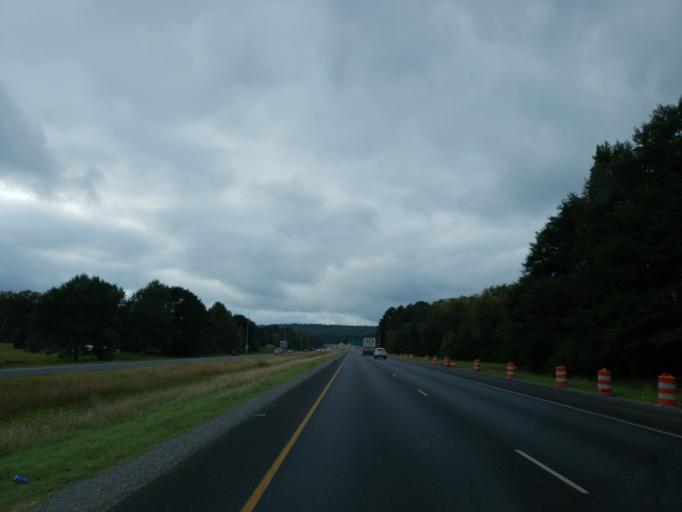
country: US
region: Alabama
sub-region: Jefferson County
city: Bessemer
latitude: 33.3389
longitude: -87.0153
